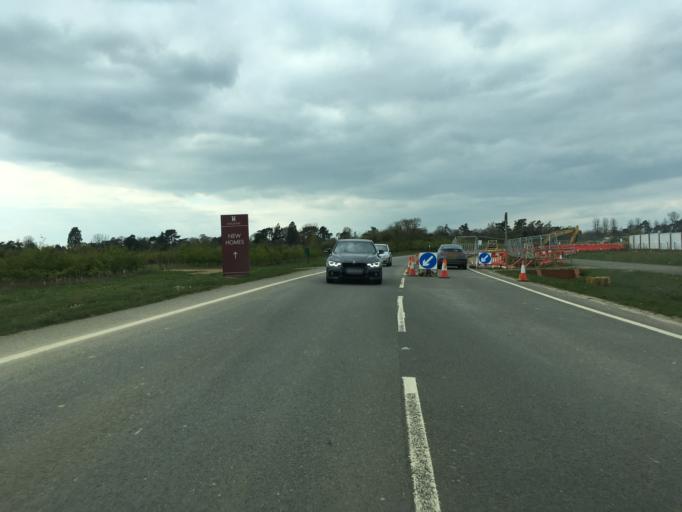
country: GB
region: England
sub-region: Oxfordshire
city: Bicester
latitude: 51.8939
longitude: -1.1809
